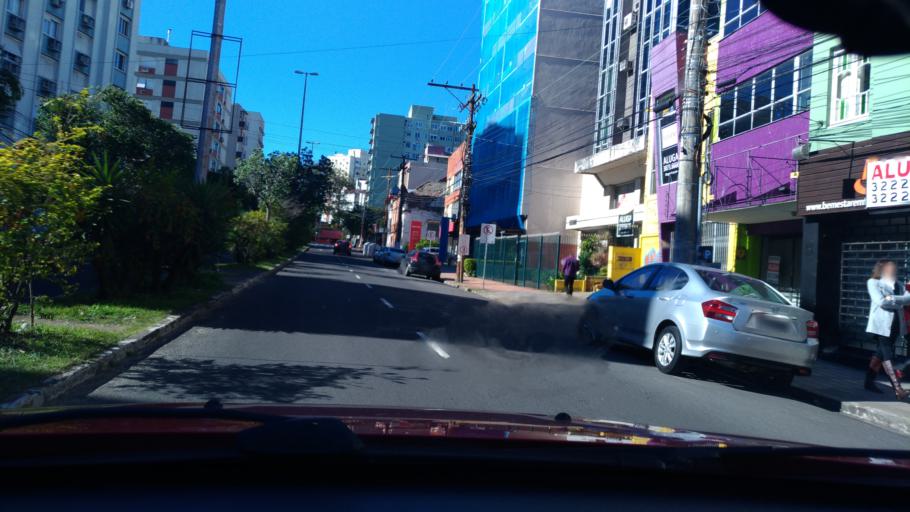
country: BR
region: Rio Grande do Sul
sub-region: Porto Alegre
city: Porto Alegre
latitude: -30.0201
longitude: -51.2068
